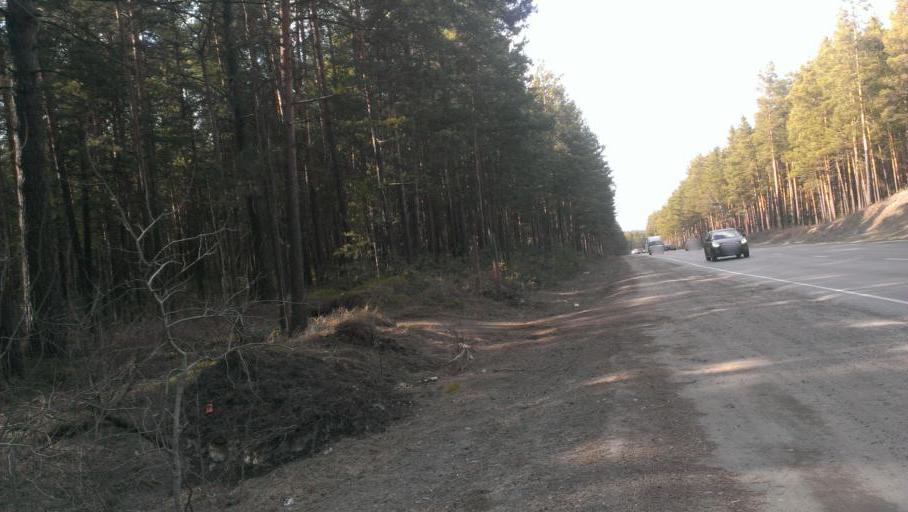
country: RU
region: Altai Krai
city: Yuzhnyy
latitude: 53.2933
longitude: 83.7064
